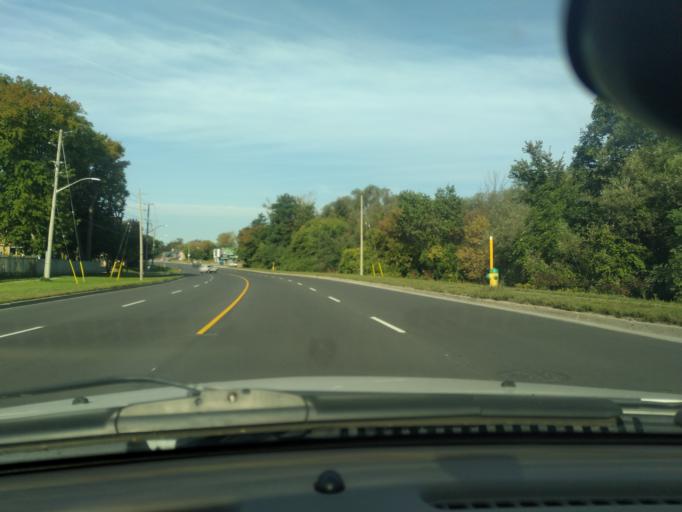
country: CA
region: Ontario
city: Barrie
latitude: 44.3714
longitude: -79.6762
